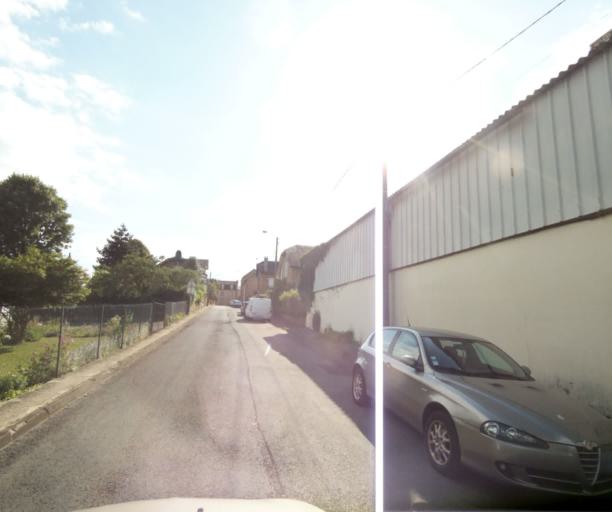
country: FR
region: Champagne-Ardenne
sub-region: Departement des Ardennes
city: Montcy-Notre-Dame
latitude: 49.7759
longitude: 4.7377
